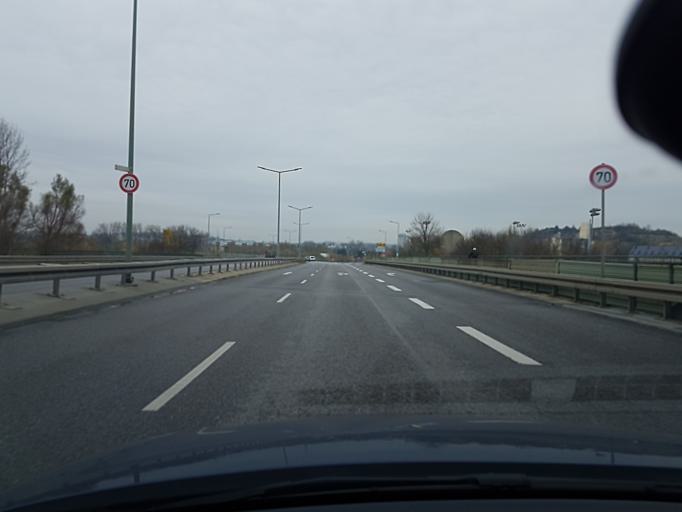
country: DE
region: Bavaria
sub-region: Upper Palatinate
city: Regensburg
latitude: 49.0234
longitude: 12.1402
